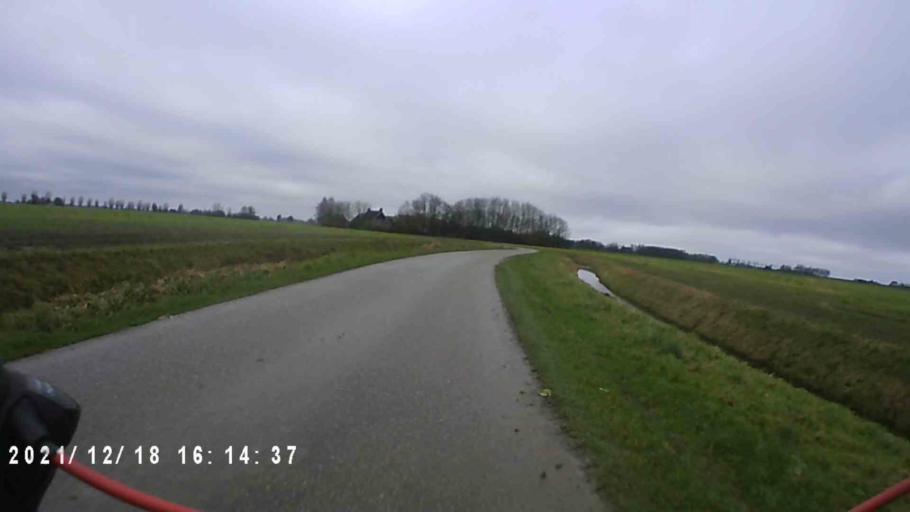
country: NL
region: Friesland
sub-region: Gemeente Dongeradeel
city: Anjum
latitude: 53.3689
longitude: 6.0650
